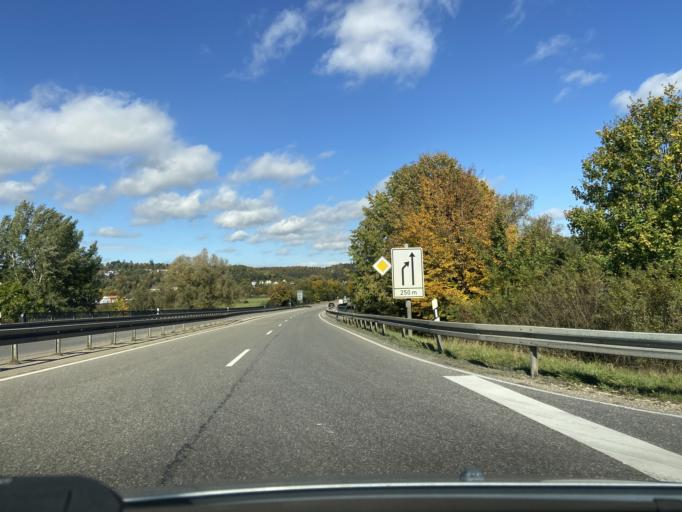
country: DE
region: Baden-Wuerttemberg
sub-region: Tuebingen Region
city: Sigmaringen
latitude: 48.0773
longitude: 9.2065
